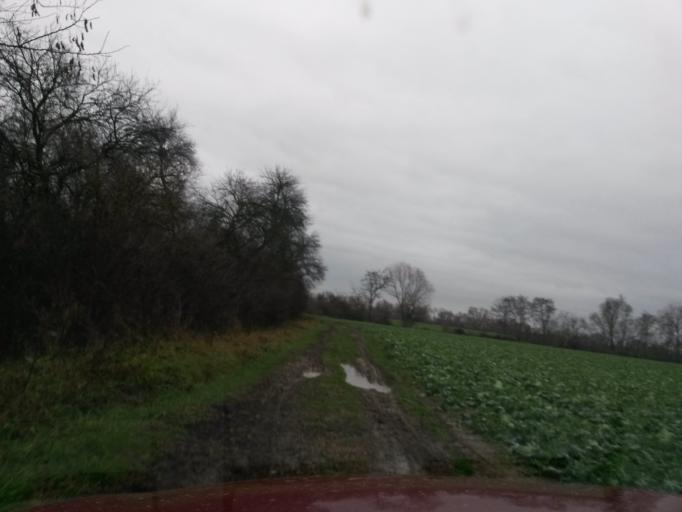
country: SK
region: Kosicky
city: Sobrance
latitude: 48.6369
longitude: 22.0882
